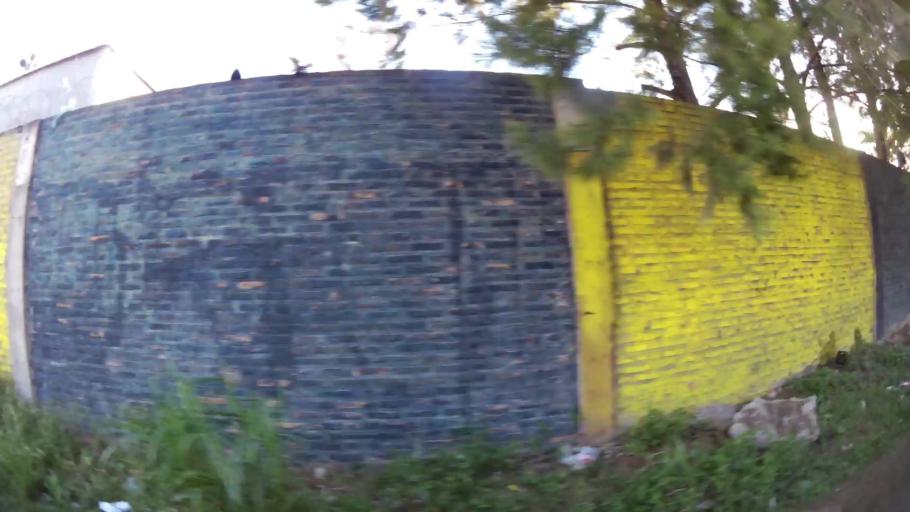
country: AR
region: Santa Fe
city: Gobernador Galvez
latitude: -32.9884
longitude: -60.6813
